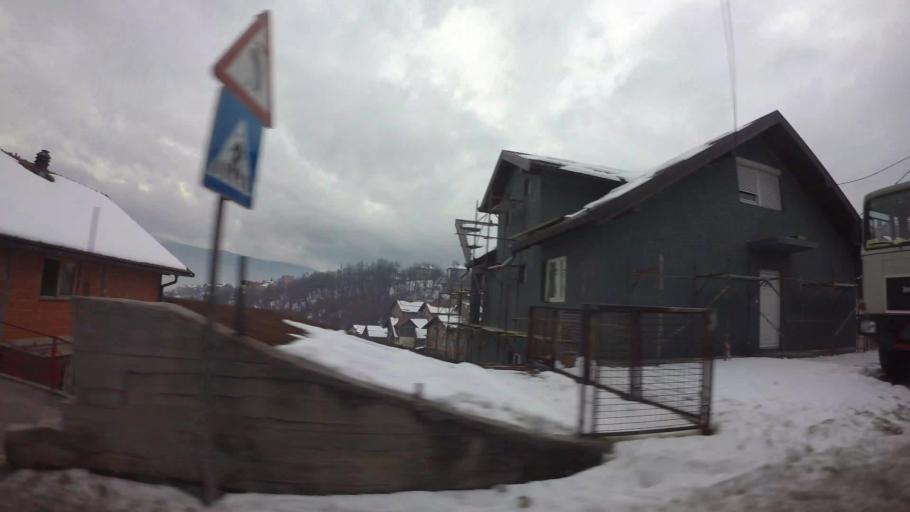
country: BA
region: Federation of Bosnia and Herzegovina
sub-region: Kanton Sarajevo
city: Sarajevo
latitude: 43.8581
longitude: 18.3568
